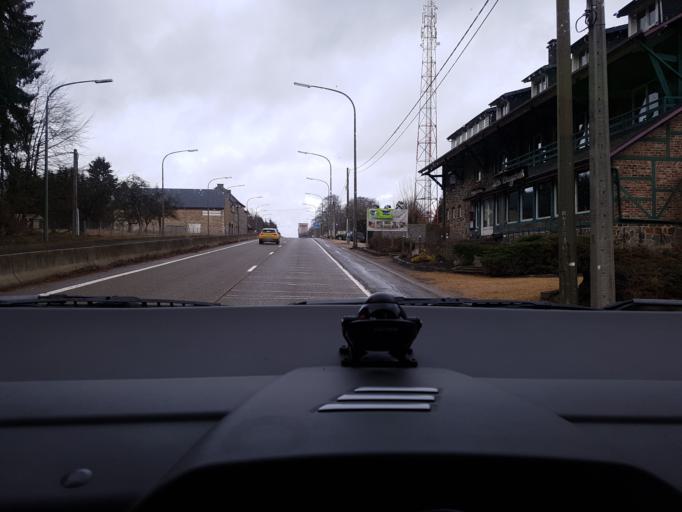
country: BE
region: Wallonia
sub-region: Province du Luxembourg
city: Tenneville
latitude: 50.1048
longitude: 5.4764
